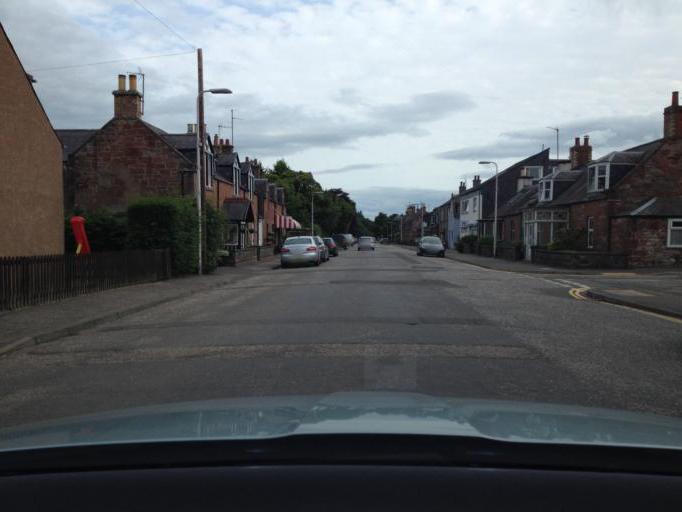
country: GB
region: Scotland
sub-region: Angus
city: Brechin
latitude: 56.8099
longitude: -2.6558
